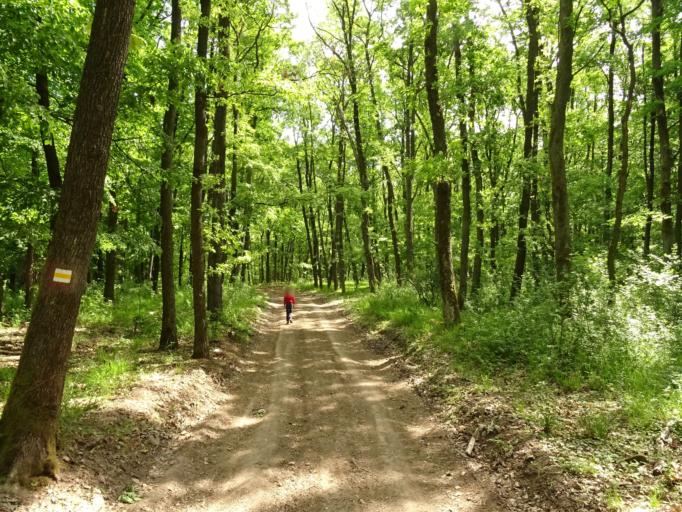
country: SK
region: Nitriansky
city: Sahy
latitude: 47.9966
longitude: 18.9393
